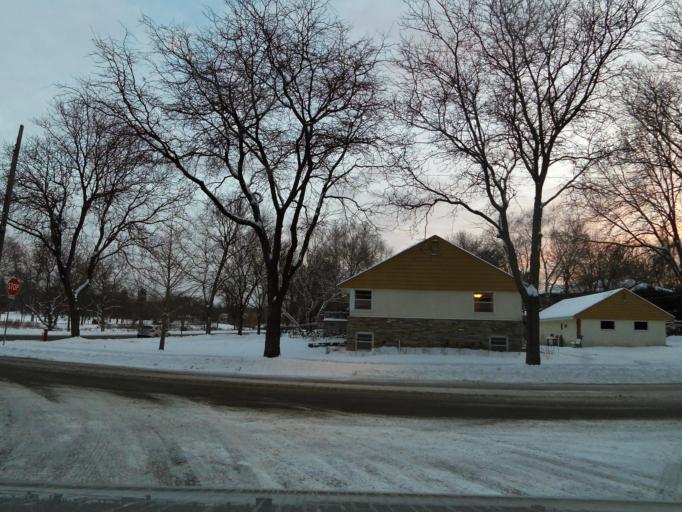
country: US
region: Minnesota
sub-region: Hennepin County
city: Saint Louis Park
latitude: 44.9379
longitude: -93.3217
